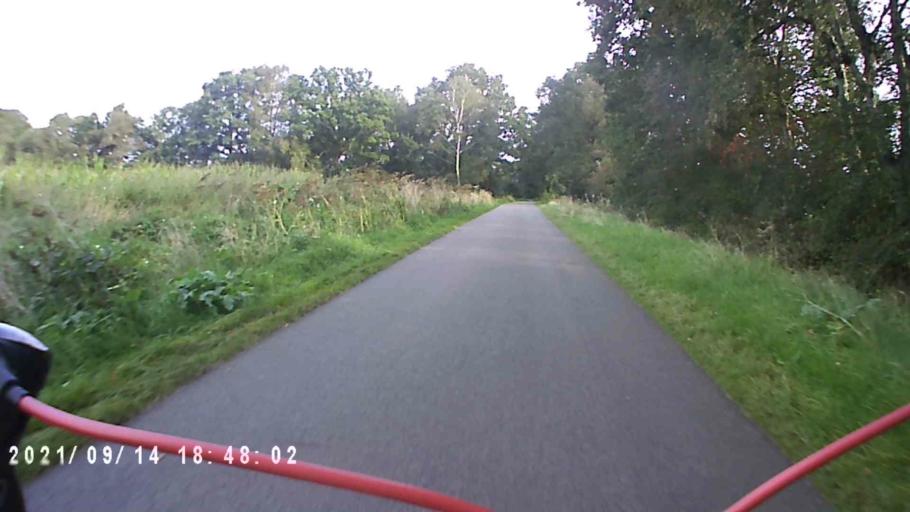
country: NL
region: Drenthe
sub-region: Gemeente Aa en Hunze
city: Anloo
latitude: 53.0282
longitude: 6.6967
